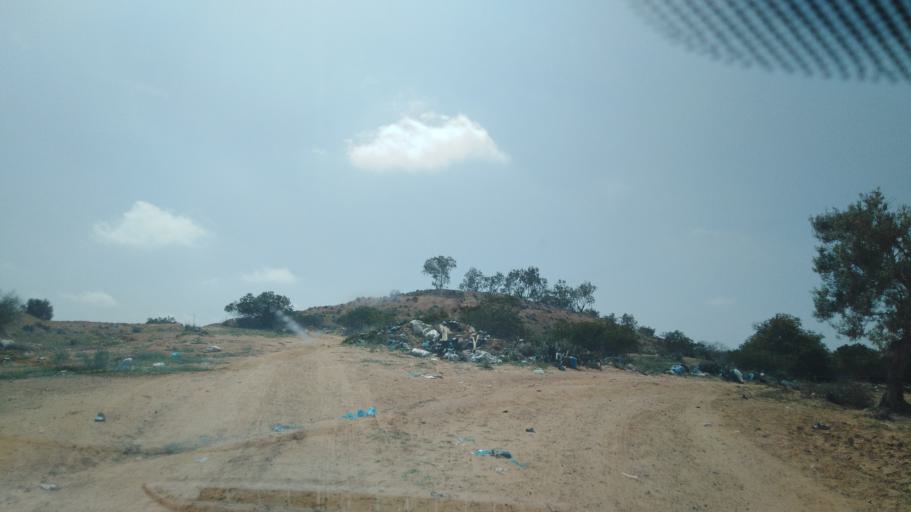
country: TN
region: Safaqis
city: Sfax
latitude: 34.7274
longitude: 10.5699
